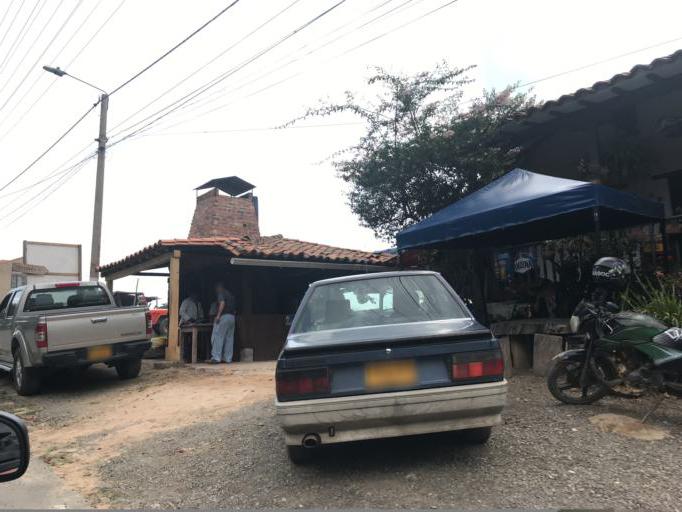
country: CO
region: Boyaca
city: Villa de Leiva
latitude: 5.6245
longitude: -73.5310
